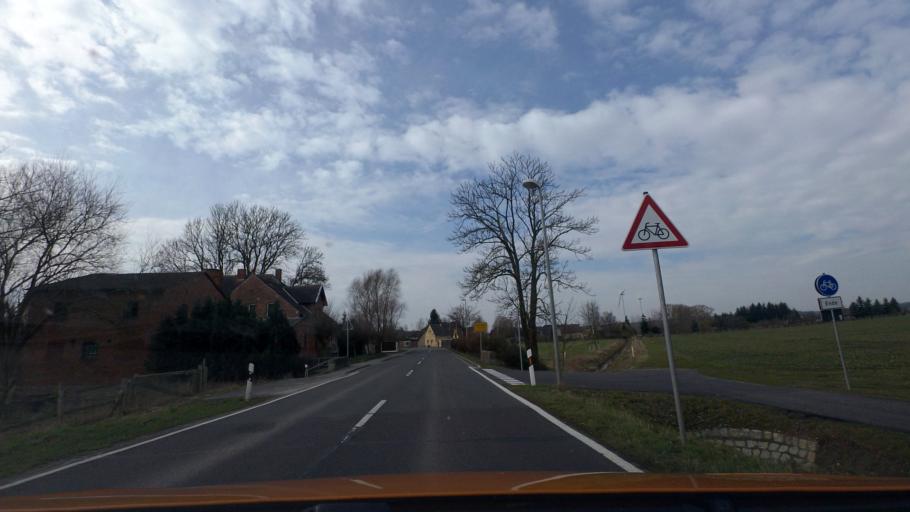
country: DE
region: Saxony-Anhalt
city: Erxleben
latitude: 52.2231
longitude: 11.2034
